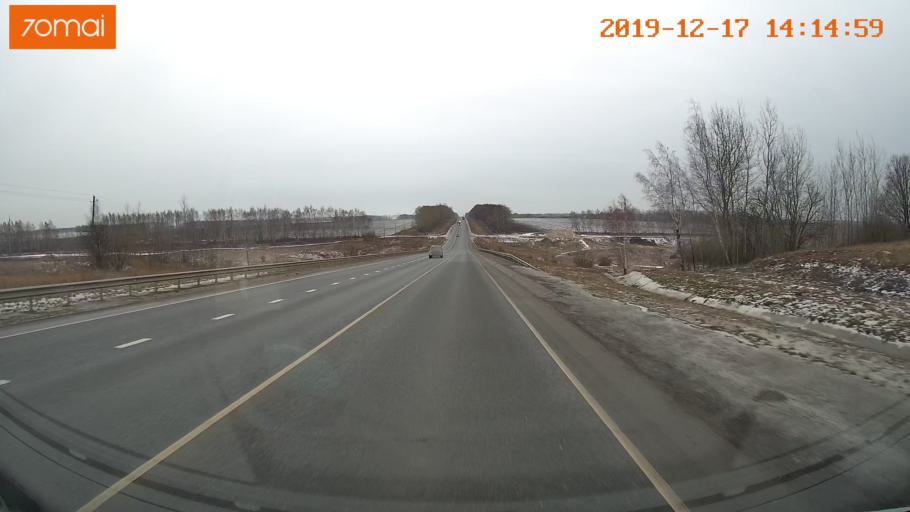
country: RU
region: Rjazan
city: Bagramovo
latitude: 54.4978
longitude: 39.4803
